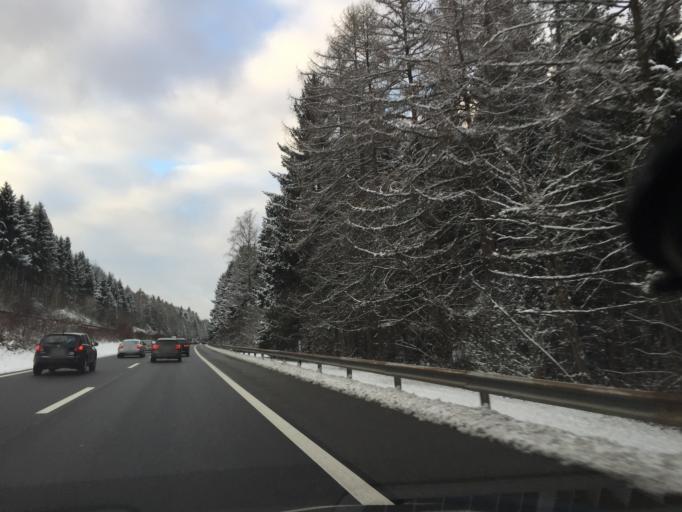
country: CH
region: Zurich
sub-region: Bezirk Horgen
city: Horgen / Scheller-Stockerstrasse
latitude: 47.2577
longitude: 8.5835
